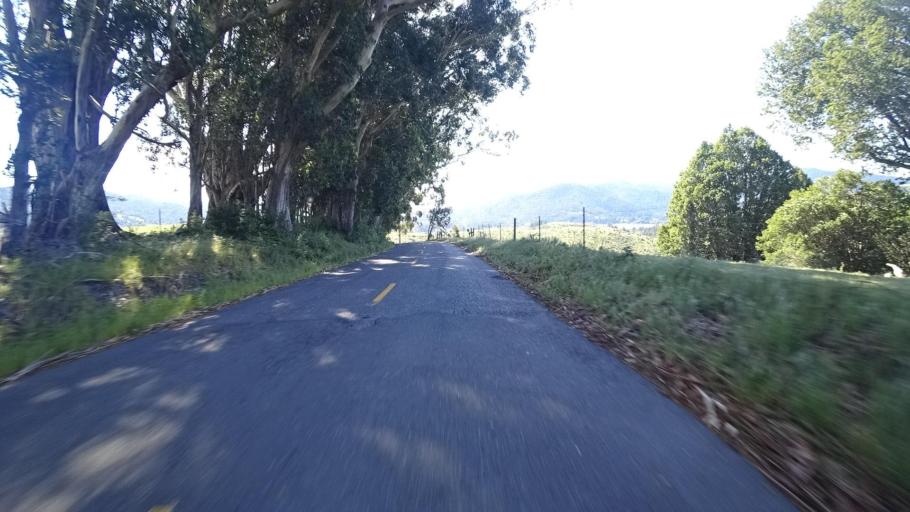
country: US
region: California
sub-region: Humboldt County
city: Ferndale
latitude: 40.3352
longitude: -124.3066
